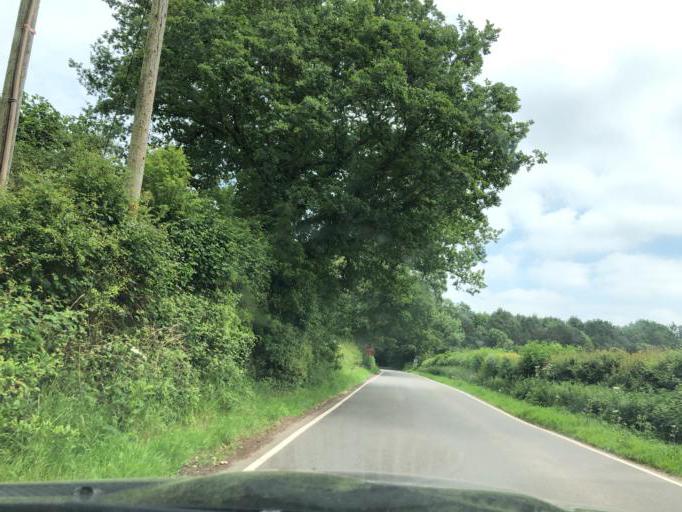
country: GB
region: England
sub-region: Warwickshire
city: Kenilworth
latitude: 52.3239
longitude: -1.5902
